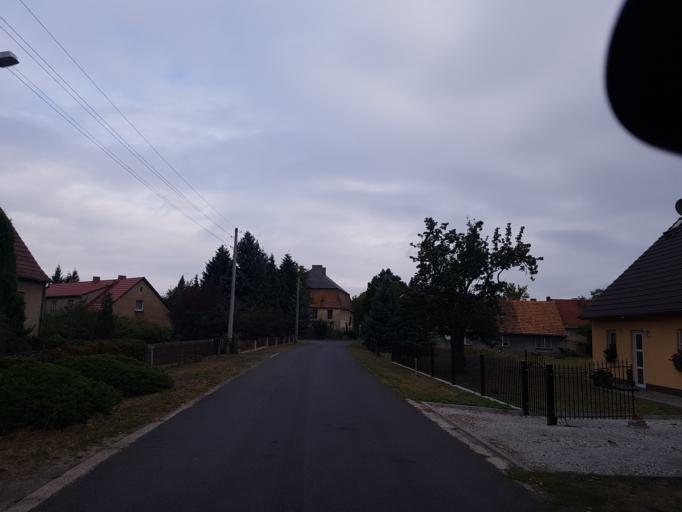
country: DE
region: Brandenburg
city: Crinitz
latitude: 51.7615
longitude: 13.8569
